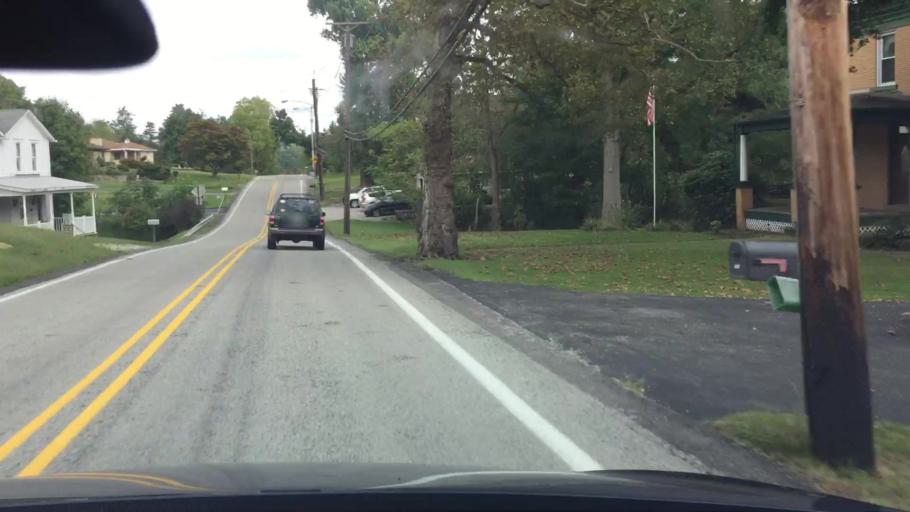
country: US
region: Pennsylvania
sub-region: Allegheny County
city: Cheswick
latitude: 40.5003
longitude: -79.7966
